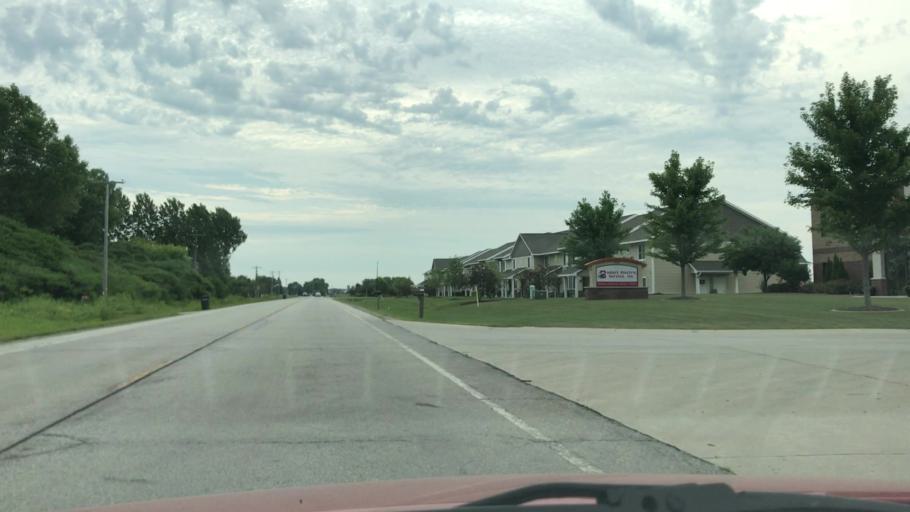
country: US
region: Wisconsin
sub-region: Brown County
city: Oneida
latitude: 44.4435
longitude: -88.1344
